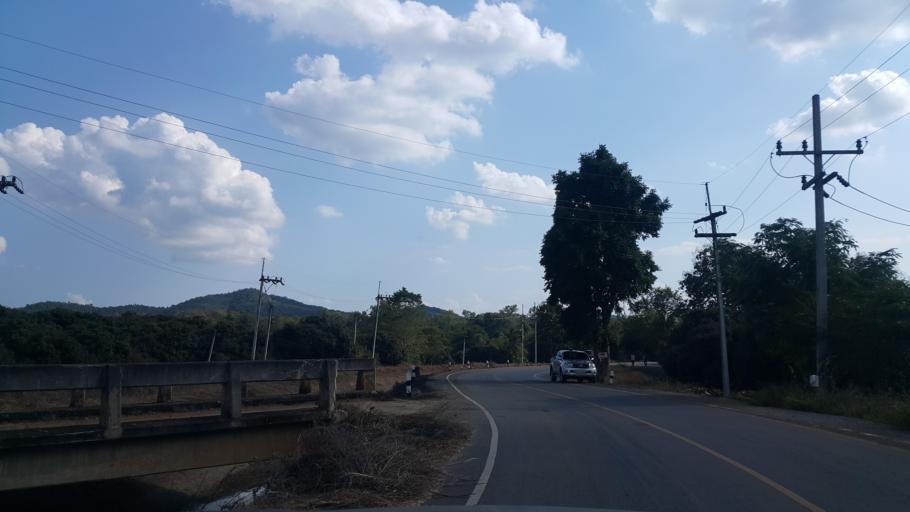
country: TH
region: Lamphun
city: Ban Thi
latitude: 18.5560
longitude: 99.1125
